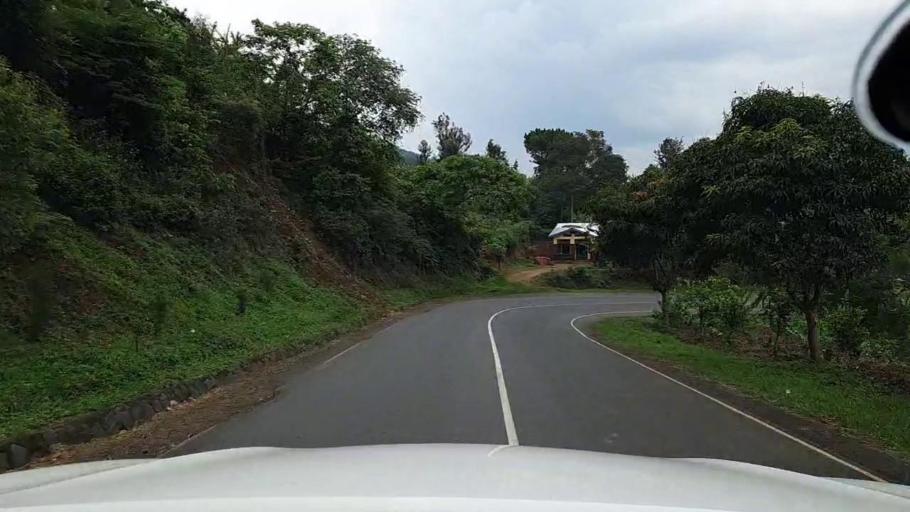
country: RW
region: Western Province
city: Cyangugu
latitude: -2.6593
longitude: 28.9751
